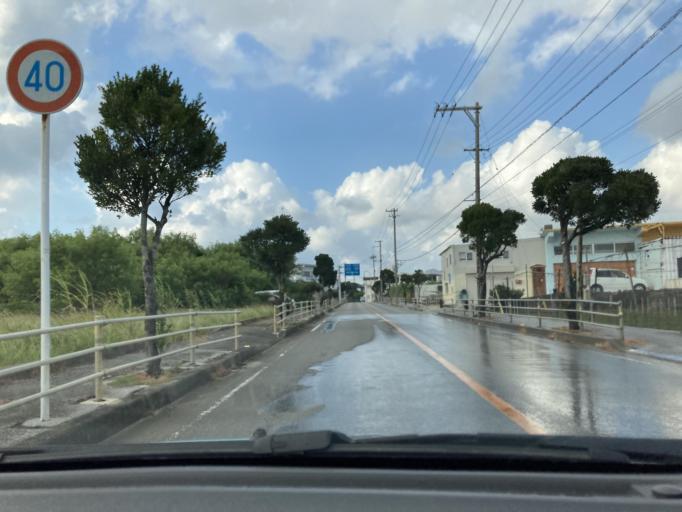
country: JP
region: Okinawa
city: Itoman
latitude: 26.1033
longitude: 127.6669
